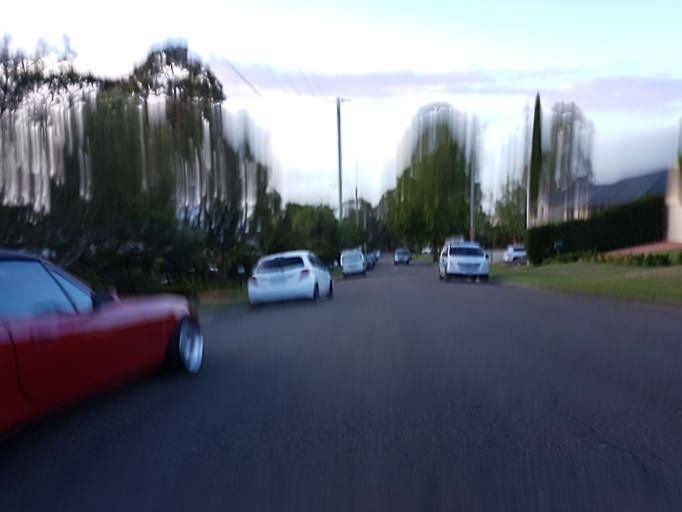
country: AU
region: New South Wales
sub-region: Warringah
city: Killarney Heights
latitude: -33.7569
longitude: 151.2296
